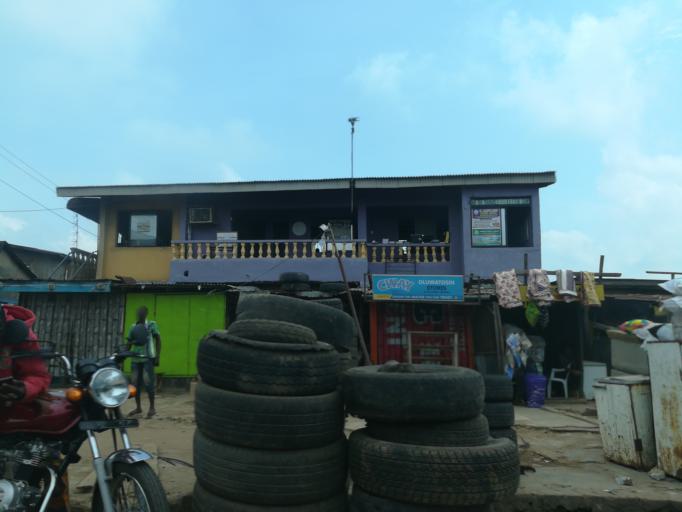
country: NG
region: Lagos
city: Ikorodu
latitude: 6.6186
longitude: 3.5063
